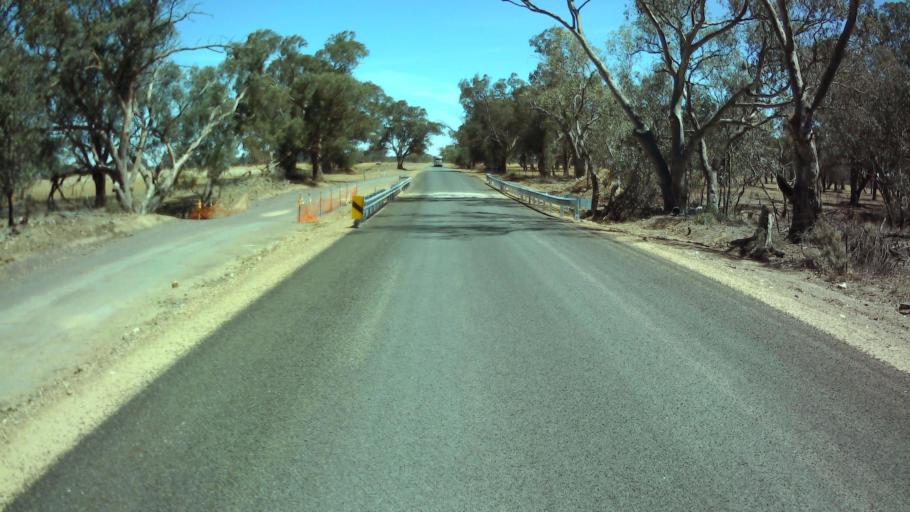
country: AU
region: New South Wales
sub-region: Weddin
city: Grenfell
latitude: -33.8429
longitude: 147.6970
